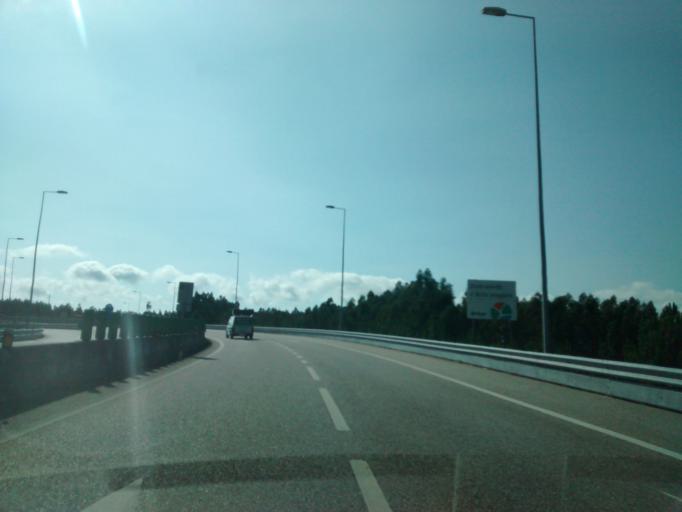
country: PT
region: Leiria
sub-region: Pombal
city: Lourical
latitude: 39.9898
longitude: -8.7923
